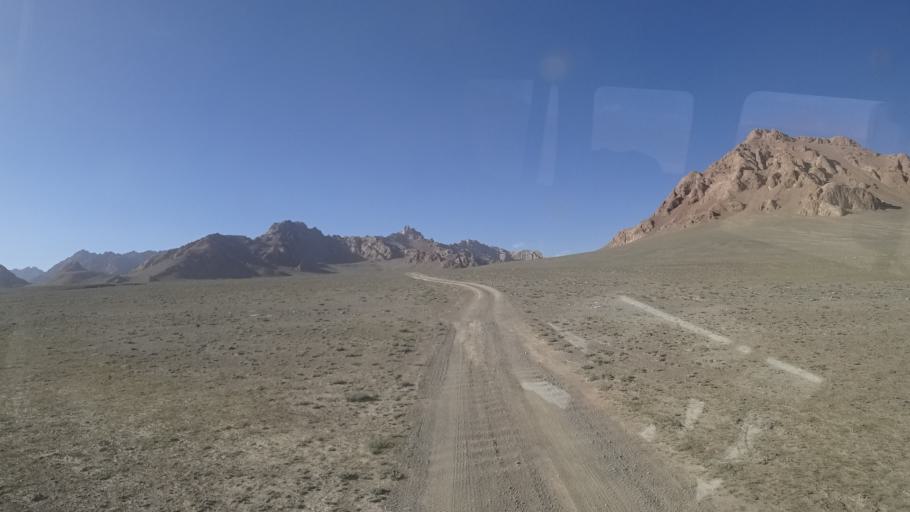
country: TJ
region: Gorno-Badakhshan
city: Murghob
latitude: 37.6698
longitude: 74.1687
